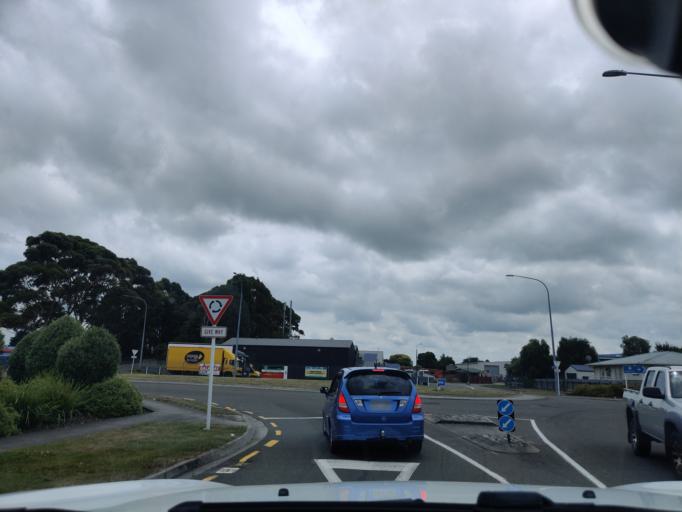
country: NZ
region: Manawatu-Wanganui
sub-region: Palmerston North City
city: Palmerston North
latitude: -40.3512
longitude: 175.5850
